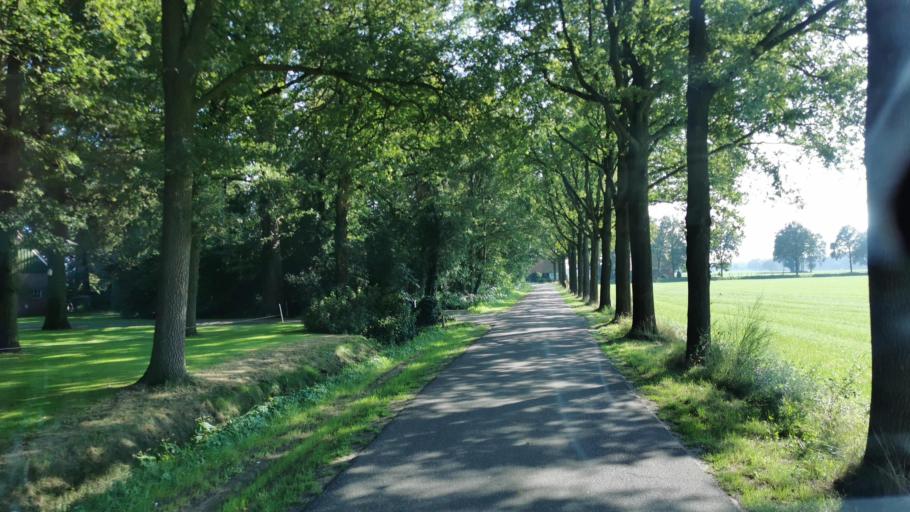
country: DE
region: Lower Saxony
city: Lage
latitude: 52.4162
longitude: 6.9492
